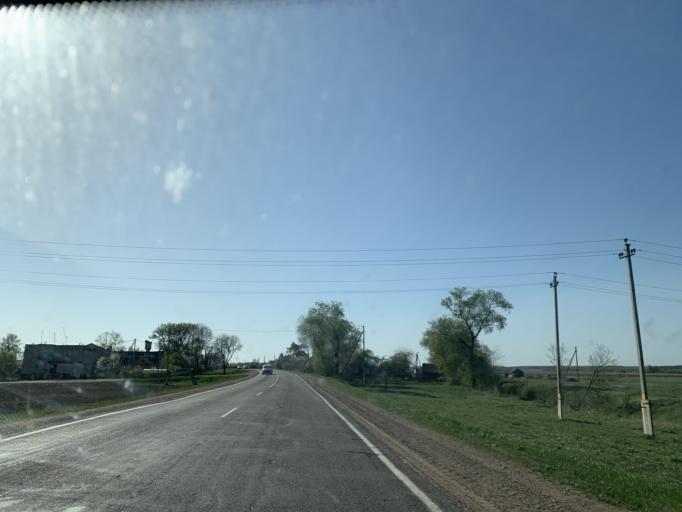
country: BY
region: Minsk
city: Nyasvizh
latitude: 53.2299
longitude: 26.7347
